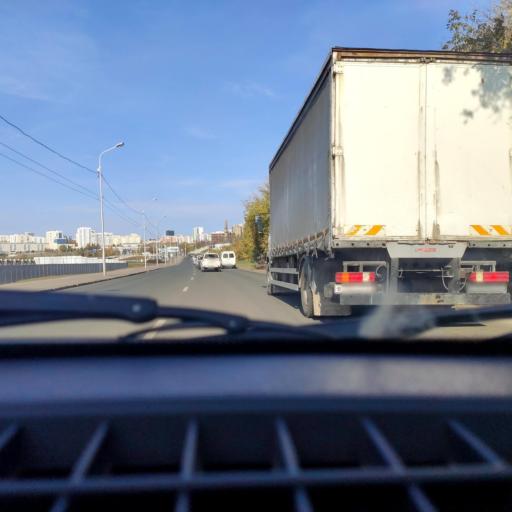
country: RU
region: Bashkortostan
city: Ufa
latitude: 54.7056
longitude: 55.9666
